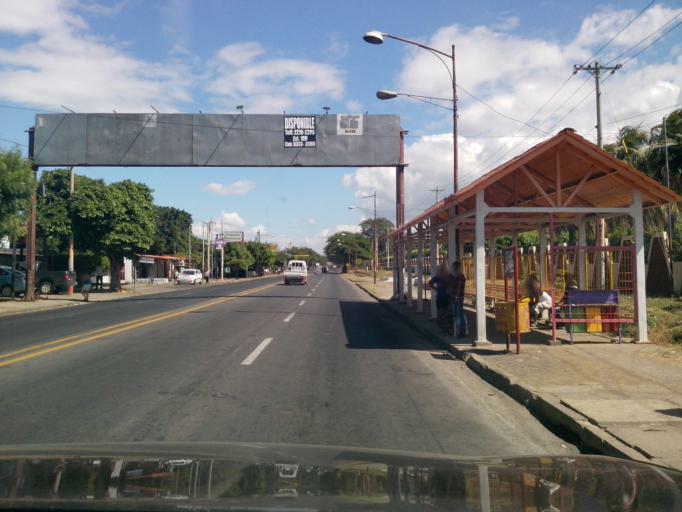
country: NI
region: Managua
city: Ciudad Sandino
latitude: 12.1383
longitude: -86.3047
